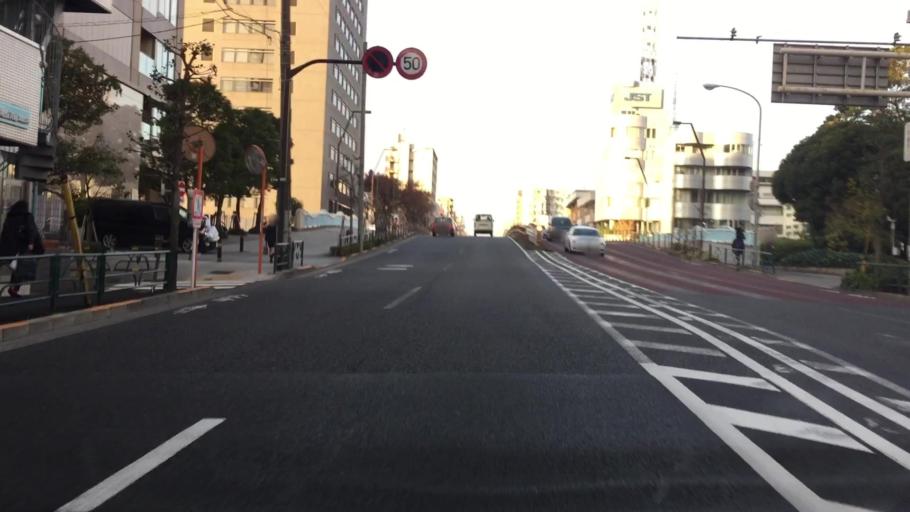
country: JP
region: Tokyo
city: Urayasu
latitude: 35.6834
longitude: 139.8064
